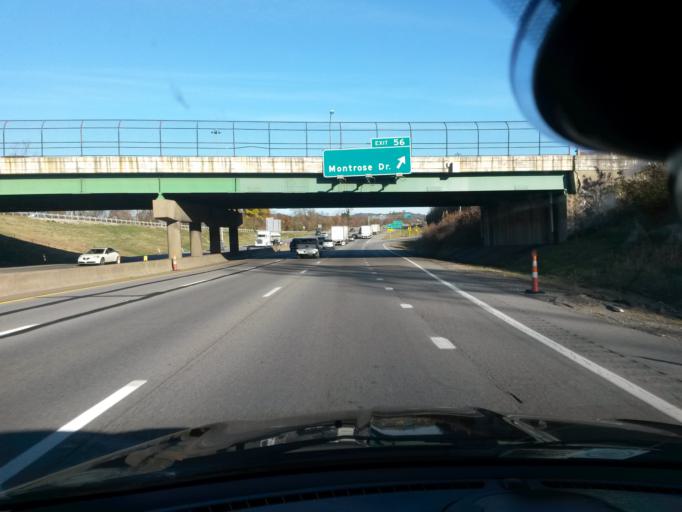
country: US
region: West Virginia
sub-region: Kanawha County
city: South Charleston
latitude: 38.3645
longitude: -81.6871
